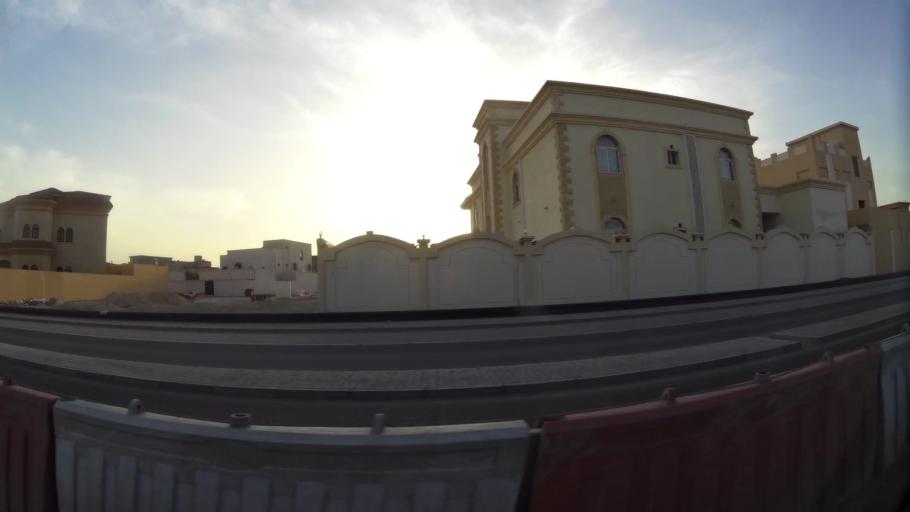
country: QA
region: Al Wakrah
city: Al Wakrah
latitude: 25.1620
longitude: 51.5904
